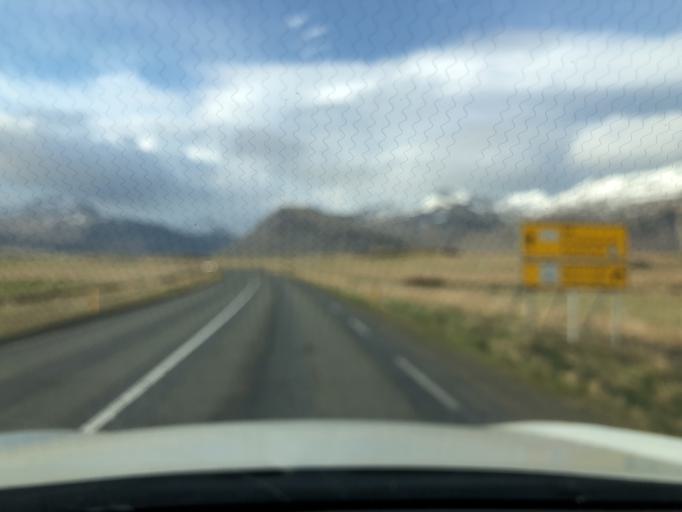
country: IS
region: East
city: Hoefn
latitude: 64.2878
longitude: -15.1833
